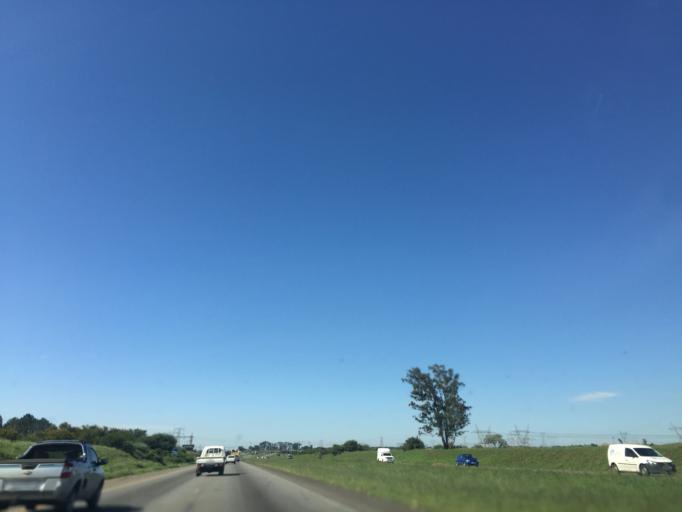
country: ZA
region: Gauteng
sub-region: Sedibeng District Municipality
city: Meyerton
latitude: -26.5873
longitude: 27.9932
